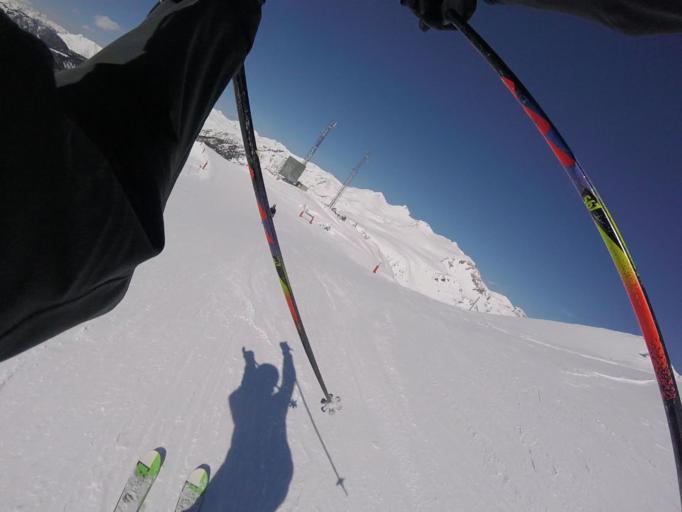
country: ES
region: Catalonia
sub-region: Provincia de Lleida
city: Espot
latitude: 42.6518
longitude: 0.9850
